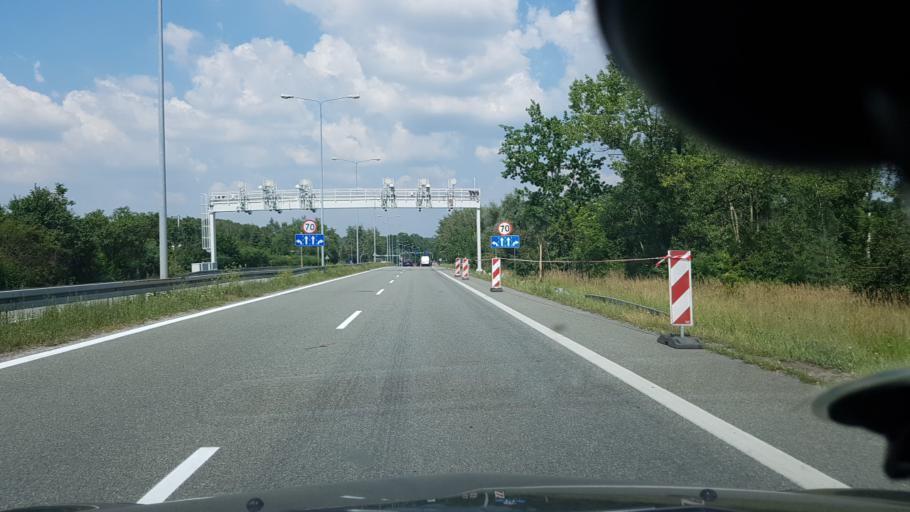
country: PL
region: Silesian Voivodeship
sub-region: Powiat mikolowski
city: Laziska Gorne
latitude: 50.1549
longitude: 18.8495
